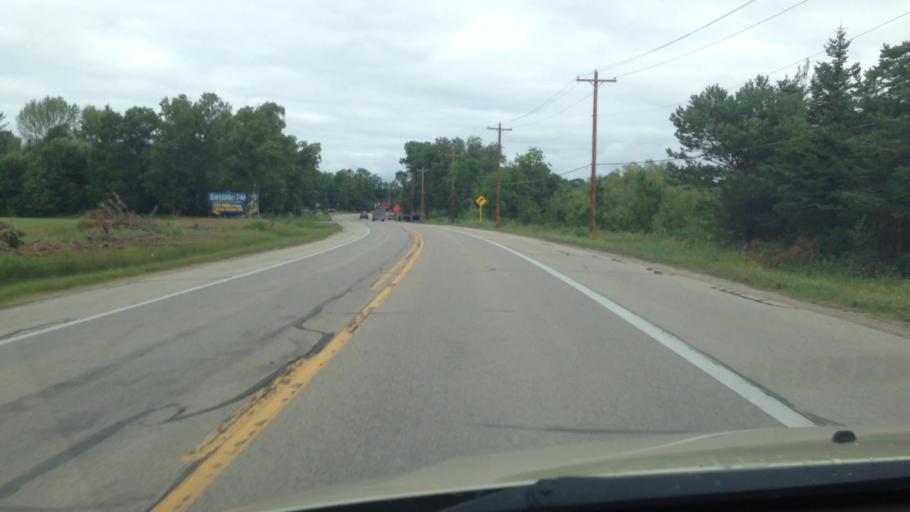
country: US
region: Michigan
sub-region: Delta County
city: Escanaba
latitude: 45.6942
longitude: -87.1006
